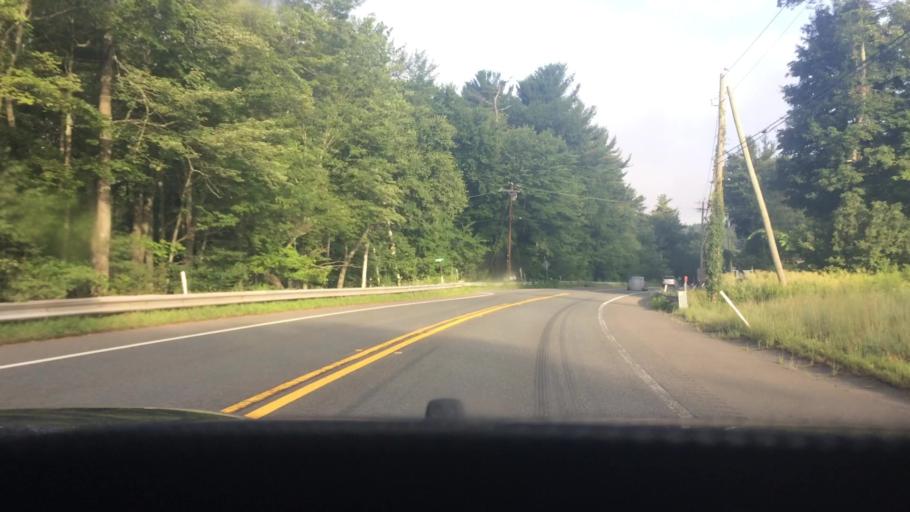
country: US
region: Massachusetts
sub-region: Franklin County
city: Turners Falls
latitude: 42.6062
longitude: -72.5287
